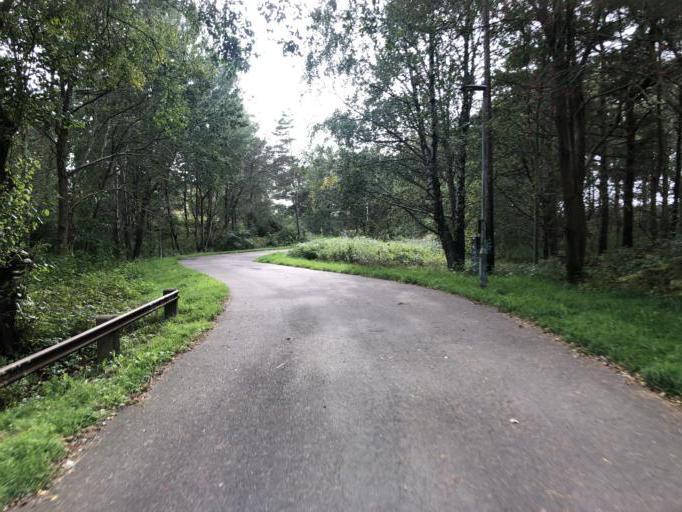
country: SE
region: Vaestra Goetaland
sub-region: Goteborg
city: Majorna
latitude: 57.7387
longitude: 11.8923
